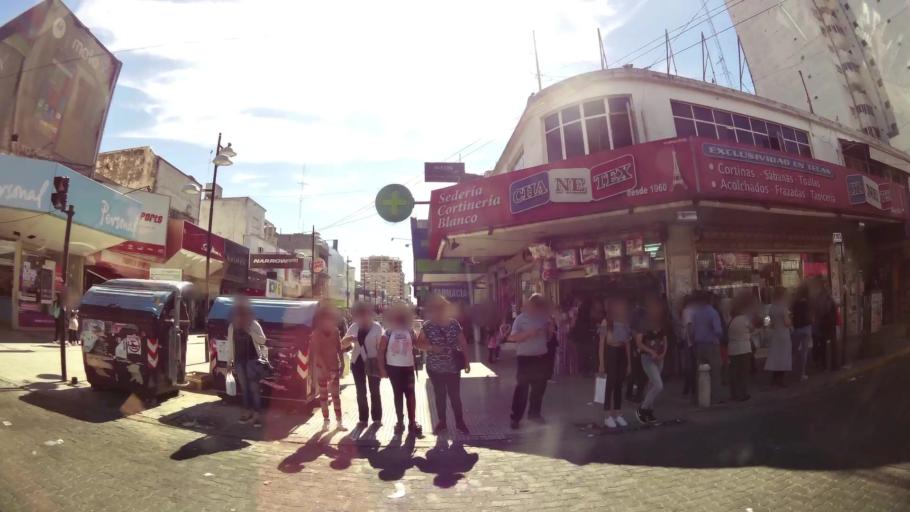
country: AR
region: Buenos Aires
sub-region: Partido de Lomas de Zamora
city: Lomas de Zamora
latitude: -34.7605
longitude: -58.4011
